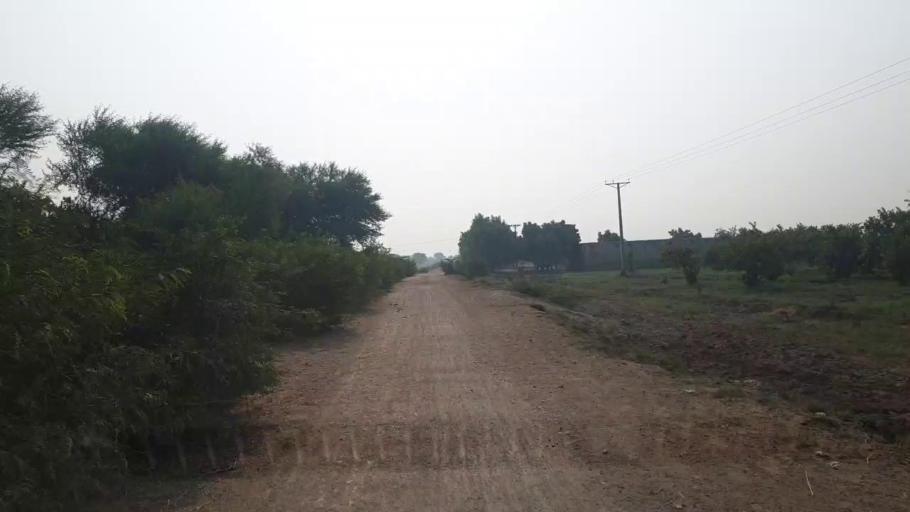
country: PK
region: Sindh
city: Tando Muhammad Khan
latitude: 25.2661
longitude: 68.5105
